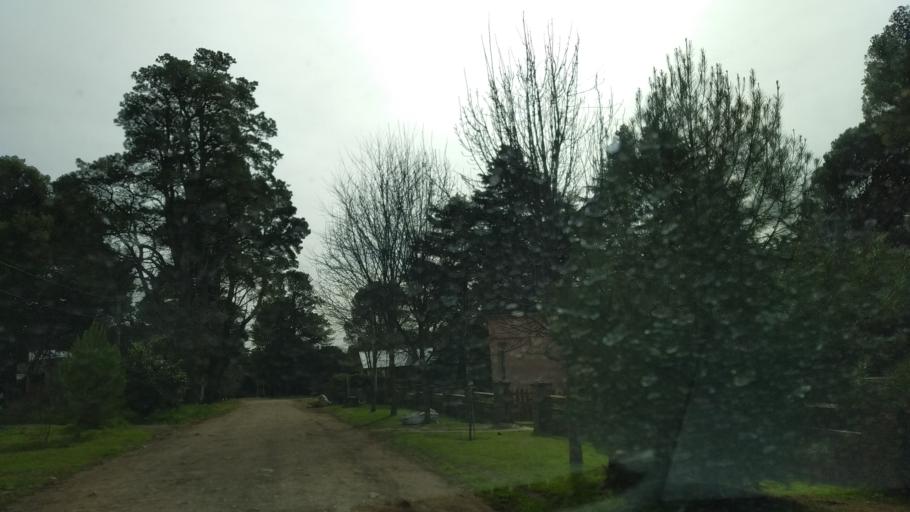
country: AR
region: Buenos Aires
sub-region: Partido de Tornquist
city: Tornquist
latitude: -38.0859
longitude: -61.9348
